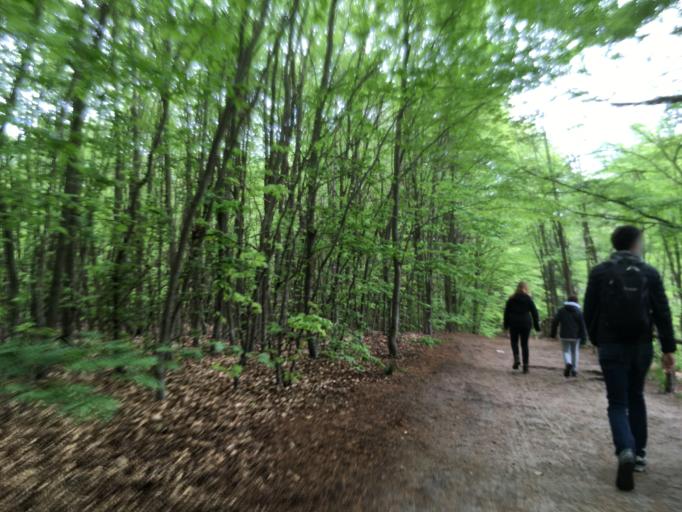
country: DE
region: Brandenburg
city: Wandlitz
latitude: 52.7482
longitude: 13.5024
